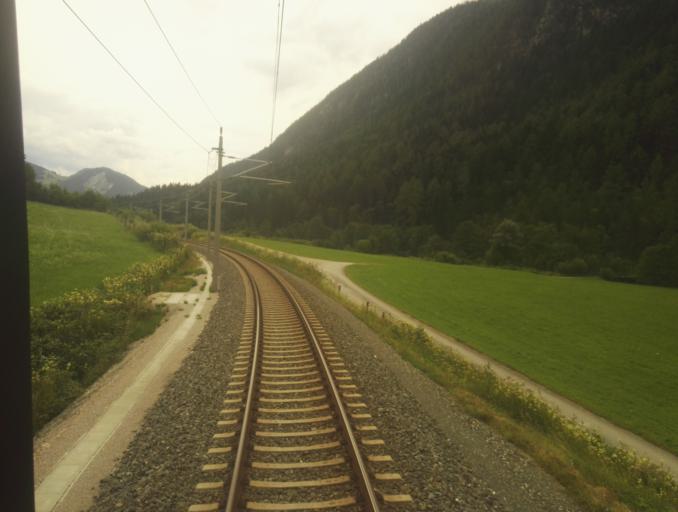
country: AT
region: Salzburg
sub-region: Politischer Bezirk Sankt Johann im Pongau
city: Forstau
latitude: 47.3974
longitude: 13.5340
